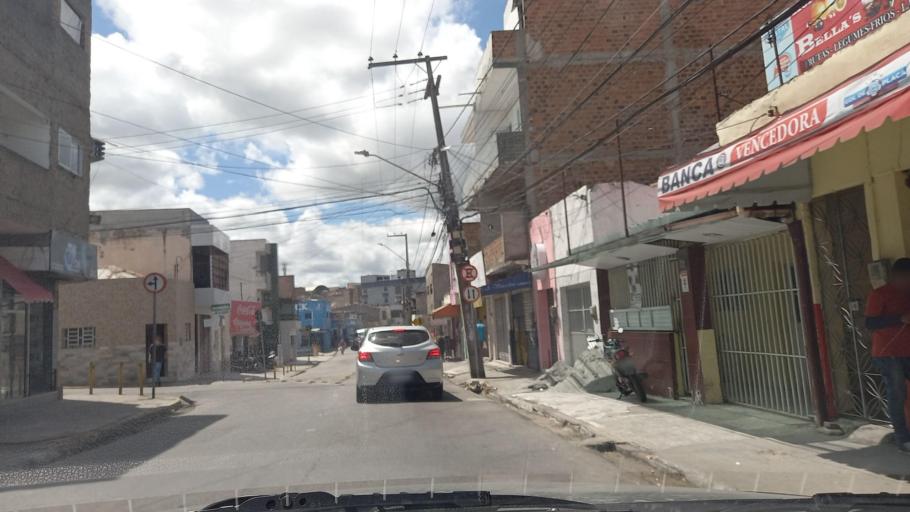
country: BR
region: Pernambuco
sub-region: Caruaru
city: Caruaru
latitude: -8.2836
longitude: -35.9639
